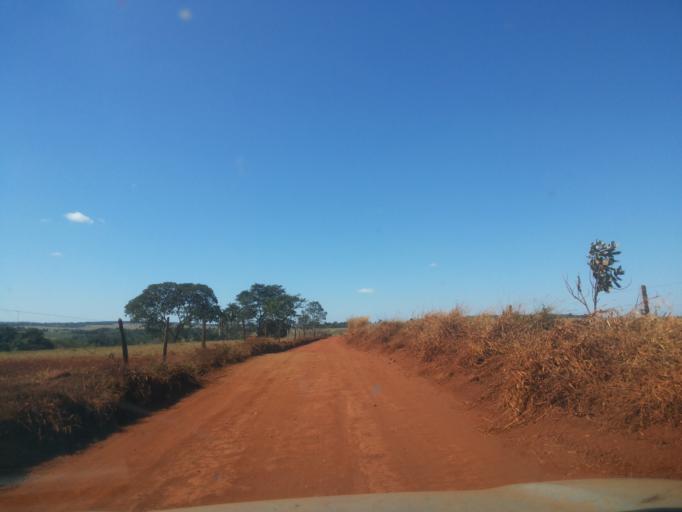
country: BR
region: Minas Gerais
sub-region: Centralina
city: Centralina
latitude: -18.7388
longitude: -49.2031
